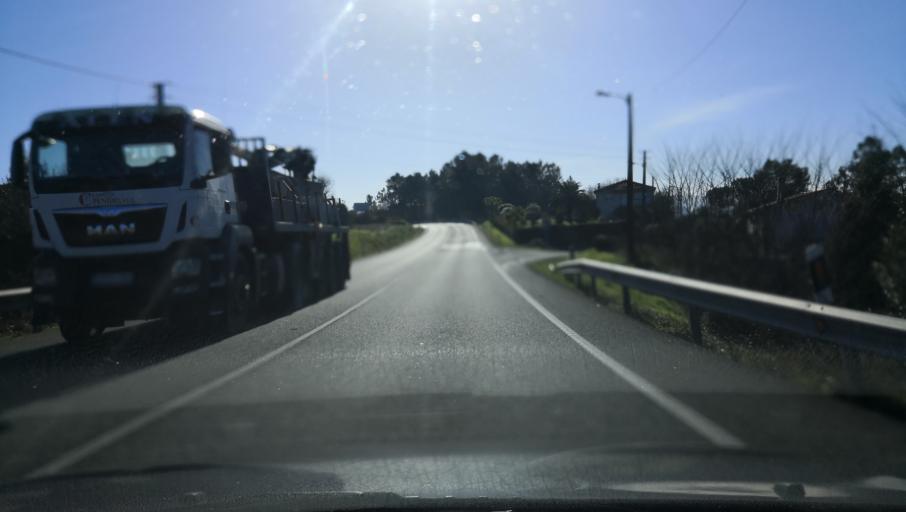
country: ES
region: Galicia
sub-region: Provincia da Coruna
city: Ribeira
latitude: 42.7826
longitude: -8.4348
